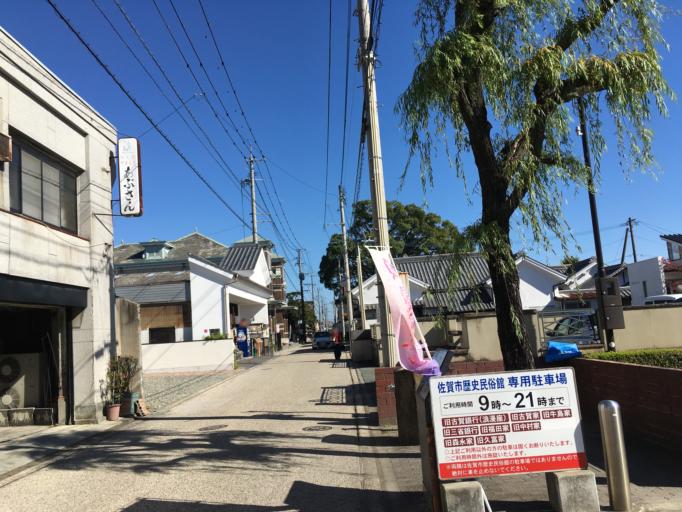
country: JP
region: Saga Prefecture
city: Saga-shi
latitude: 33.2539
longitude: 130.3060
